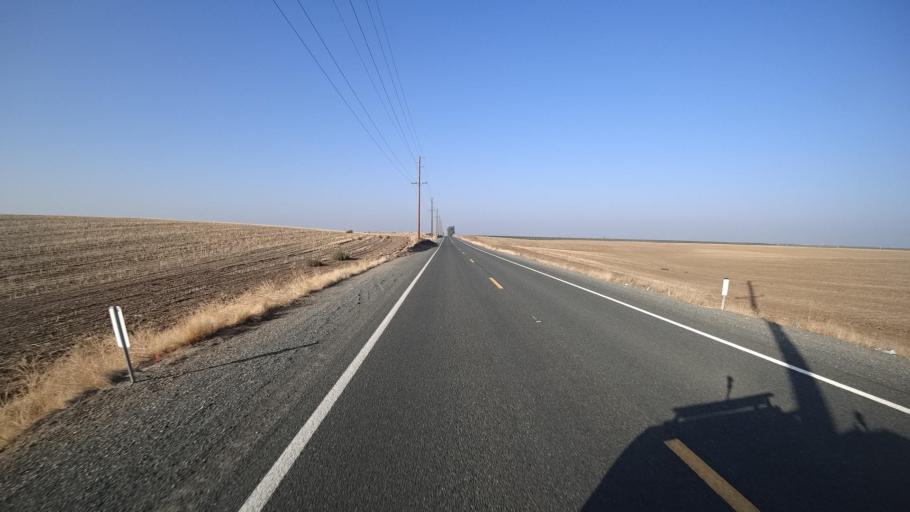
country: US
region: California
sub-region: Tulare County
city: Richgrove
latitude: 35.7619
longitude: -119.0736
